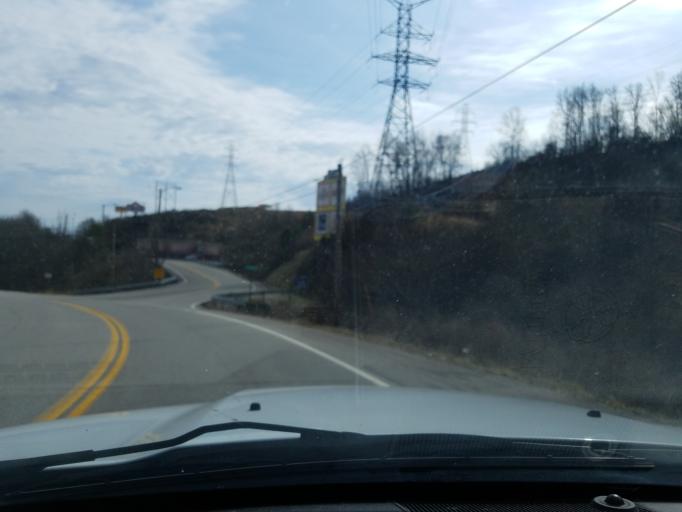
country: US
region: West Virginia
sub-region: Kanawha County
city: Cross Lanes
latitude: 38.4118
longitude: -81.7984
